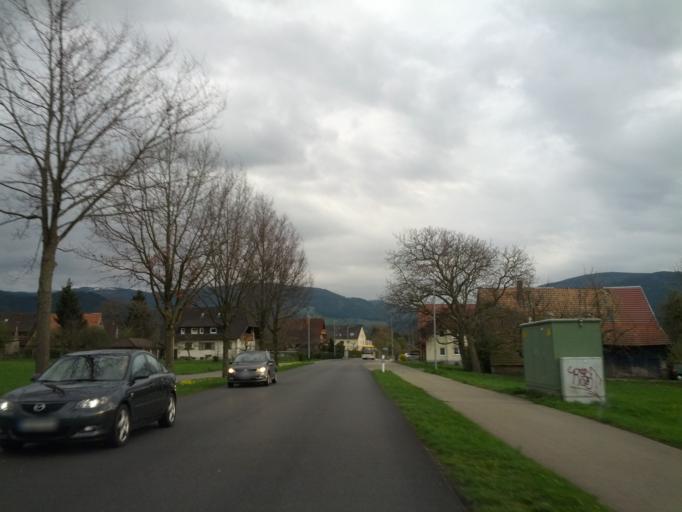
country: DE
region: Baden-Wuerttemberg
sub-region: Freiburg Region
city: Stegen
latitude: 47.9792
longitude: 7.9627
